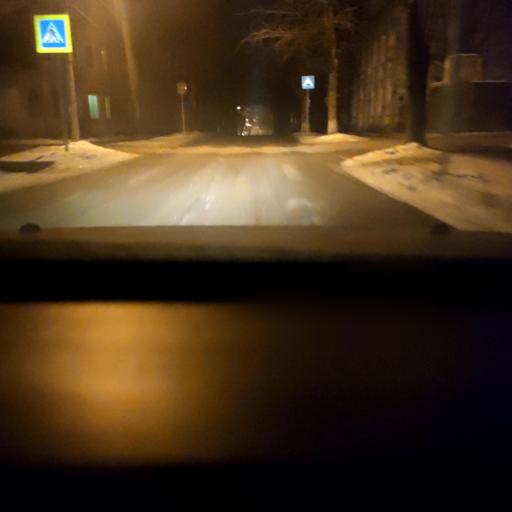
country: RU
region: Perm
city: Perm
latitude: 58.1060
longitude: 56.3070
